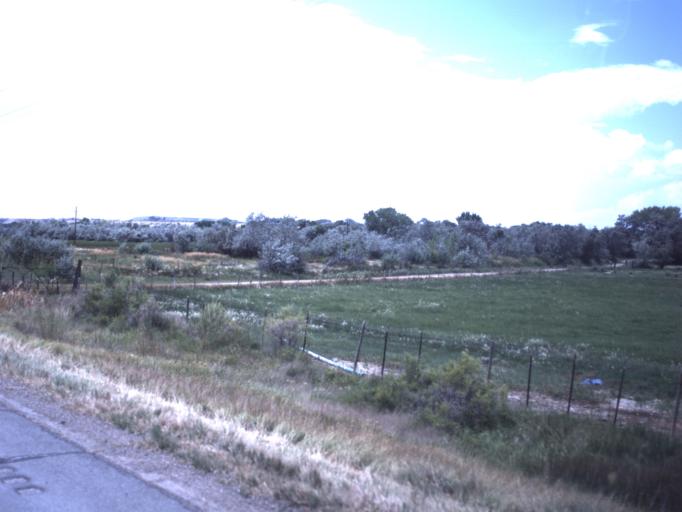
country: US
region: Utah
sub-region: Duchesne County
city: Roosevelt
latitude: 40.1690
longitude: -110.1448
